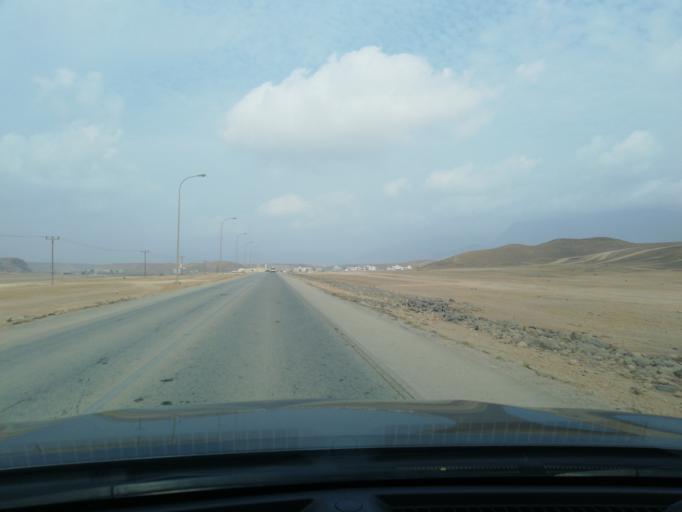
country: OM
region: Zufar
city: Salalah
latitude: 16.9609
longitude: 53.8765
